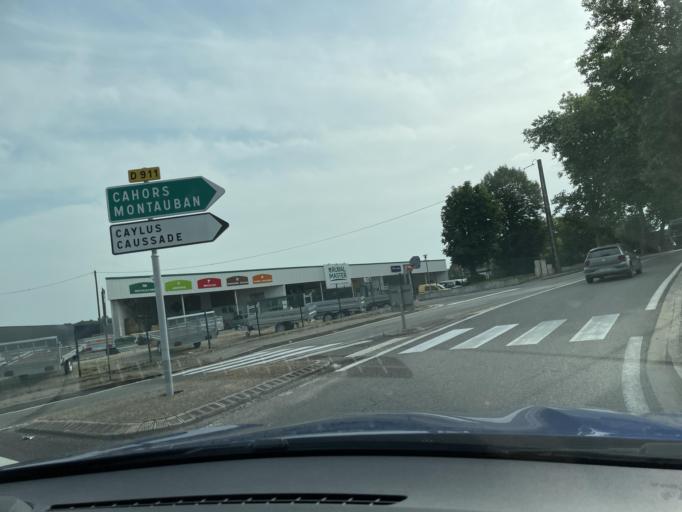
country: FR
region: Midi-Pyrenees
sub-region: Departement de l'Aveyron
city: Villefranche-de-Rouergue
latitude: 44.3608
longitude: 2.0030
